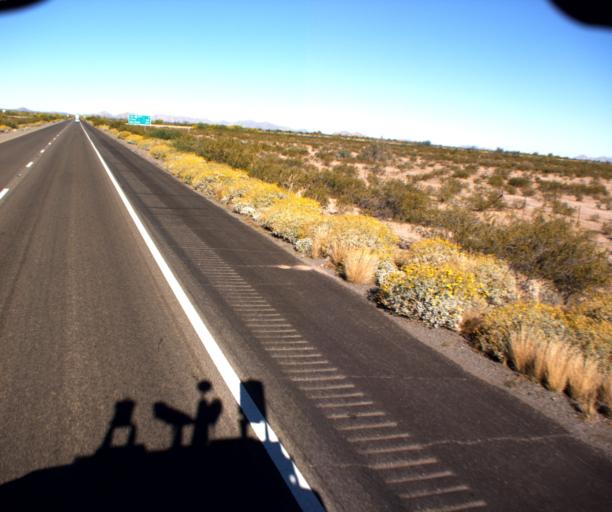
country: US
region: Arizona
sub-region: Pinal County
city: Casa Grande
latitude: 32.8286
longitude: -111.9744
